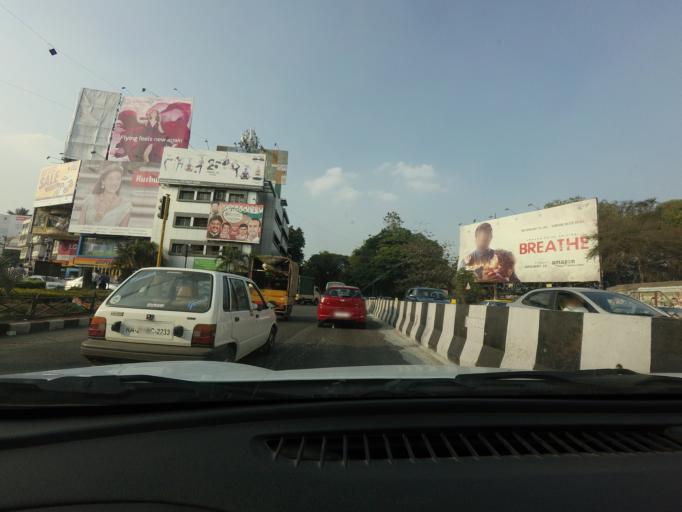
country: IN
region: Karnataka
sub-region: Bangalore Urban
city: Bangalore
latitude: 13.0034
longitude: 77.5841
